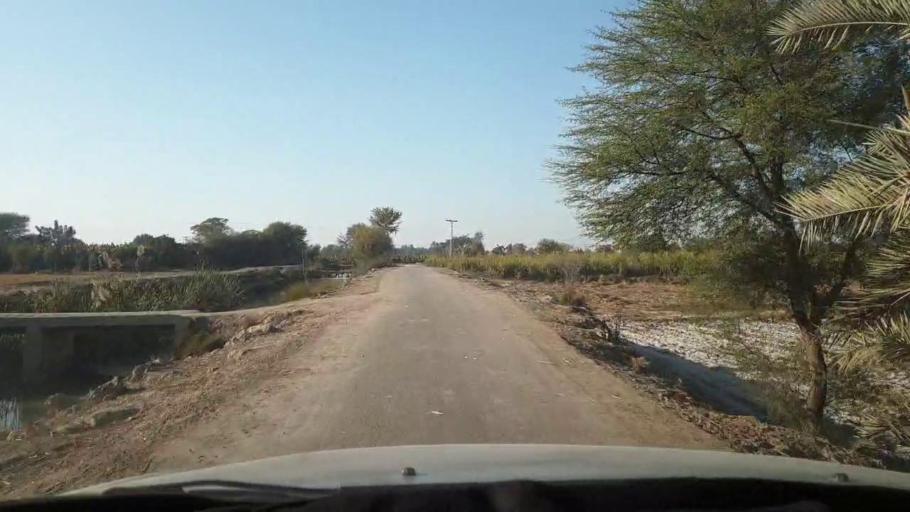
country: PK
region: Sindh
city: Adilpur
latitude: 27.9374
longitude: 69.2588
